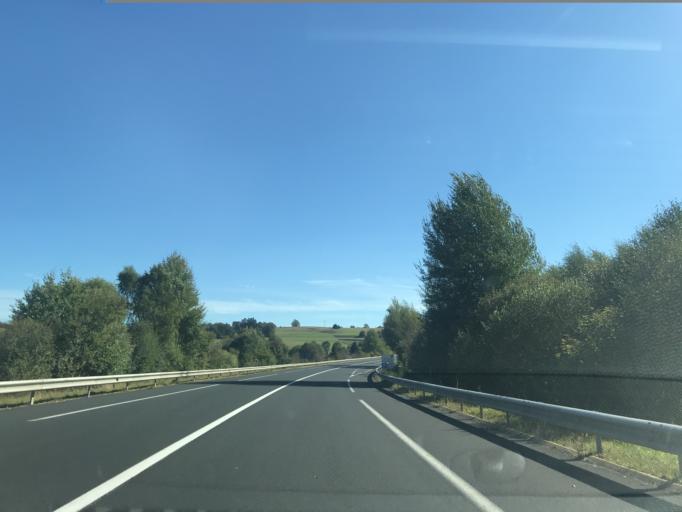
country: FR
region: Auvergne
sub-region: Departement du Puy-de-Dome
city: Saint-Sauves-d'Auvergne
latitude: 45.6673
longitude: 2.7221
